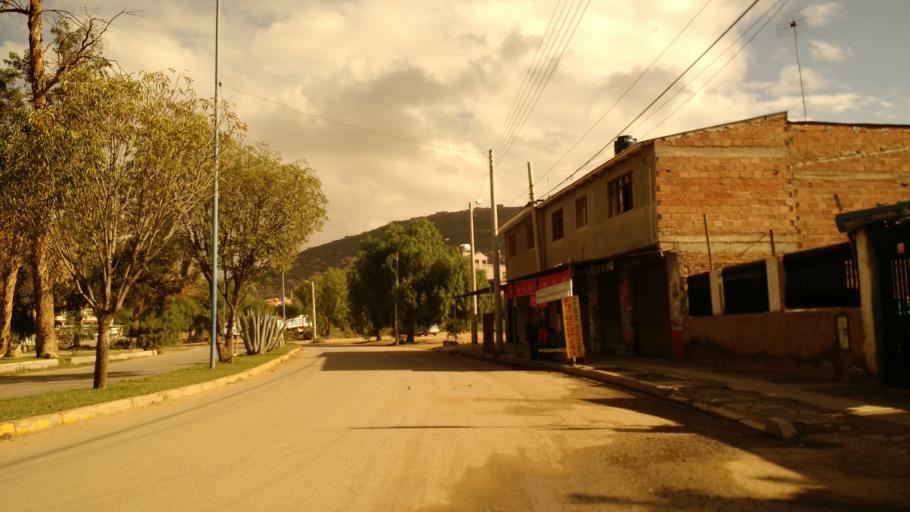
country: BO
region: Cochabamba
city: Cochabamba
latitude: -17.4462
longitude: -66.1409
